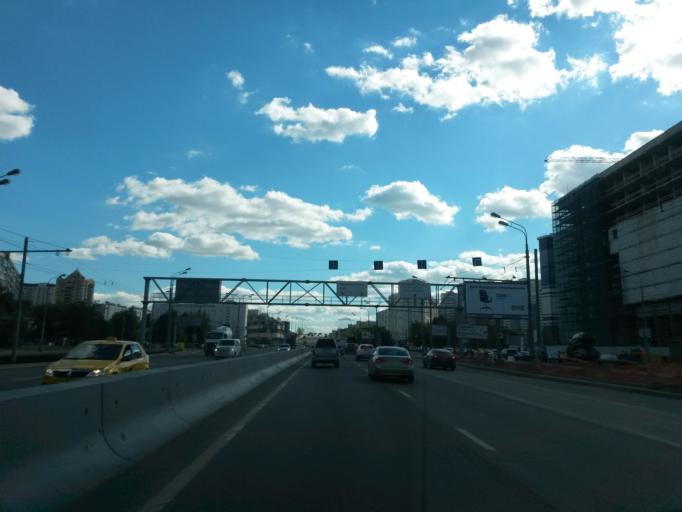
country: RU
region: Moscow
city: Chertanovo Yuzhnoye
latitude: 55.5991
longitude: 37.6038
